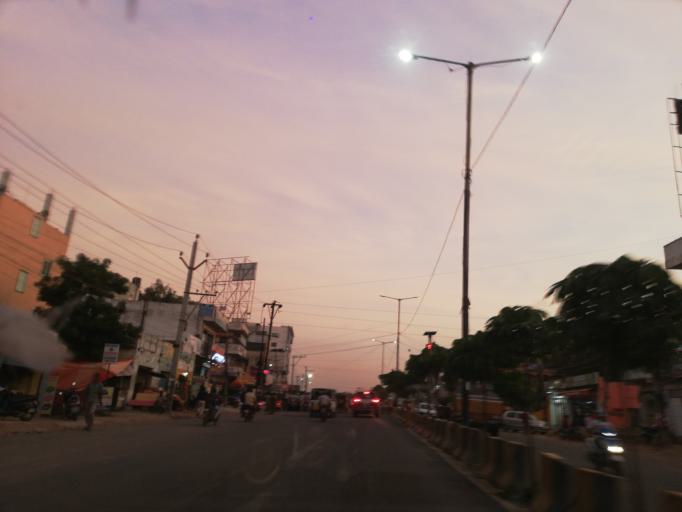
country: IN
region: Telangana
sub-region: Rangareddi
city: Kukatpalli
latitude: 17.4987
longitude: 78.3619
